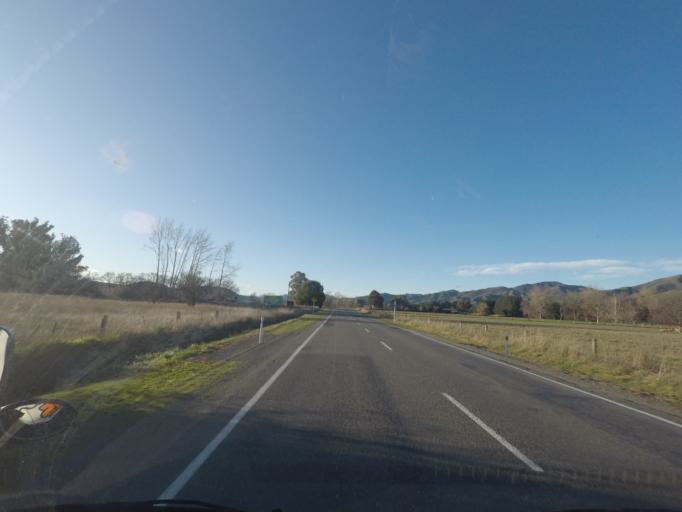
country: NZ
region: Canterbury
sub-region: Kaikoura District
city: Kaikoura
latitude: -42.7122
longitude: 173.2914
